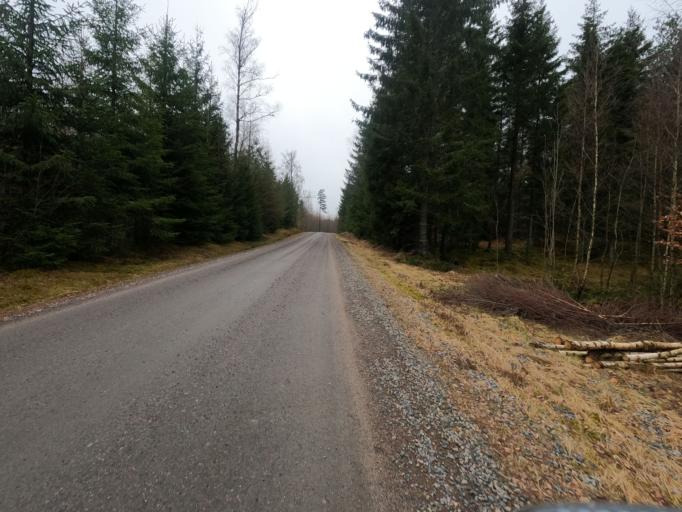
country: SE
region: Kronoberg
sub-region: Markaryds Kommun
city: Stromsnasbruk
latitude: 56.8120
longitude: 13.5694
